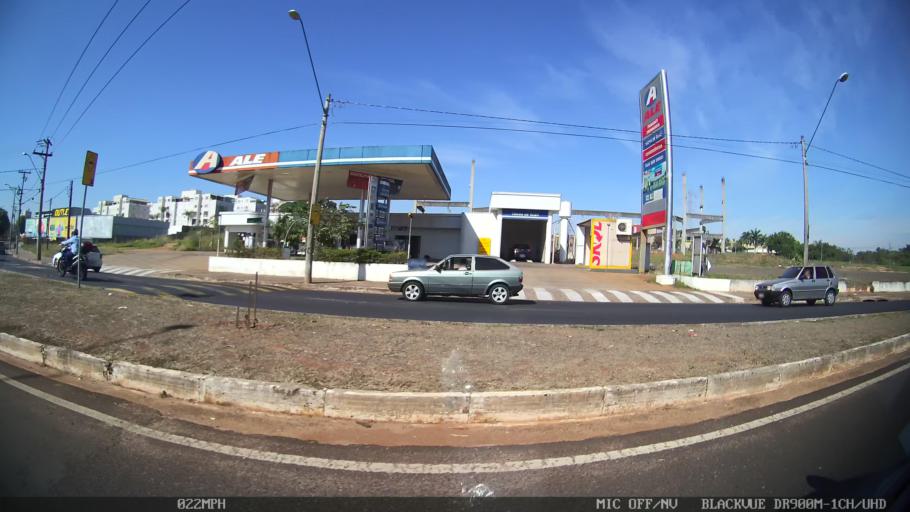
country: BR
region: Sao Paulo
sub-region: Sao Jose Do Rio Preto
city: Sao Jose do Rio Preto
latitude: -20.7836
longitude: -49.3817
